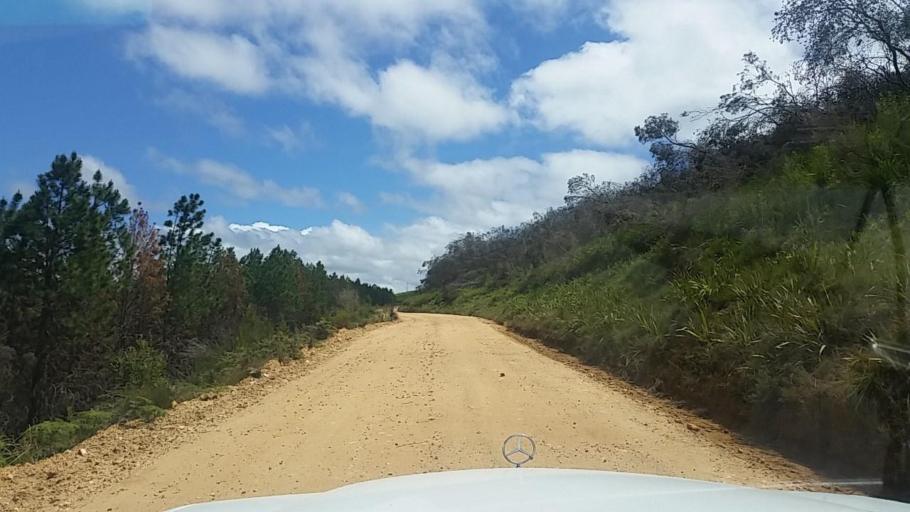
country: ZA
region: Western Cape
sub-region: Eden District Municipality
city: Knysna
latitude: -33.8917
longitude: 23.1679
